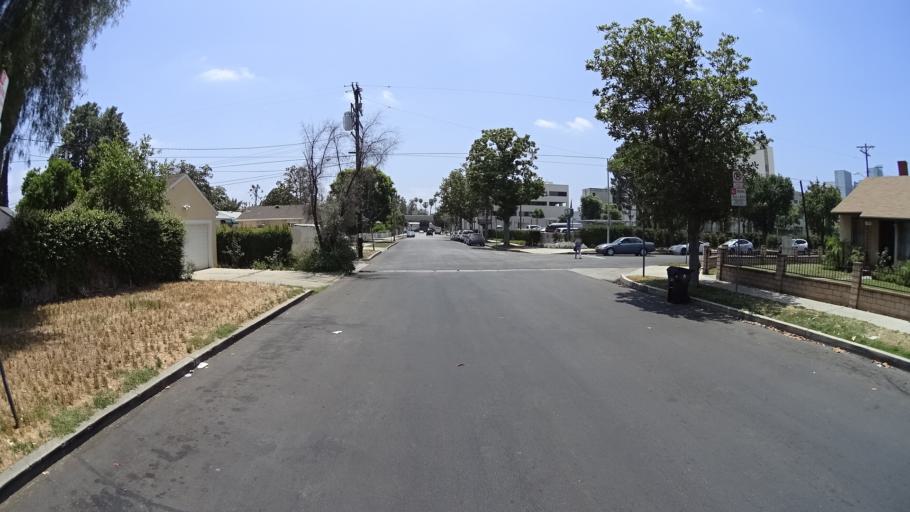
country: US
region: California
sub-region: Los Angeles County
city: Van Nuys
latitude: 34.1960
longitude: -118.4619
